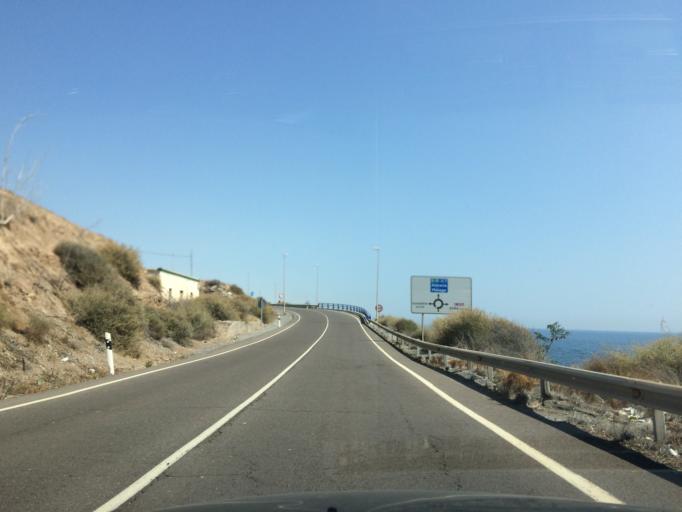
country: ES
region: Andalusia
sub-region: Provincia de Almeria
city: Adra
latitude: 36.7474
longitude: -3.0583
